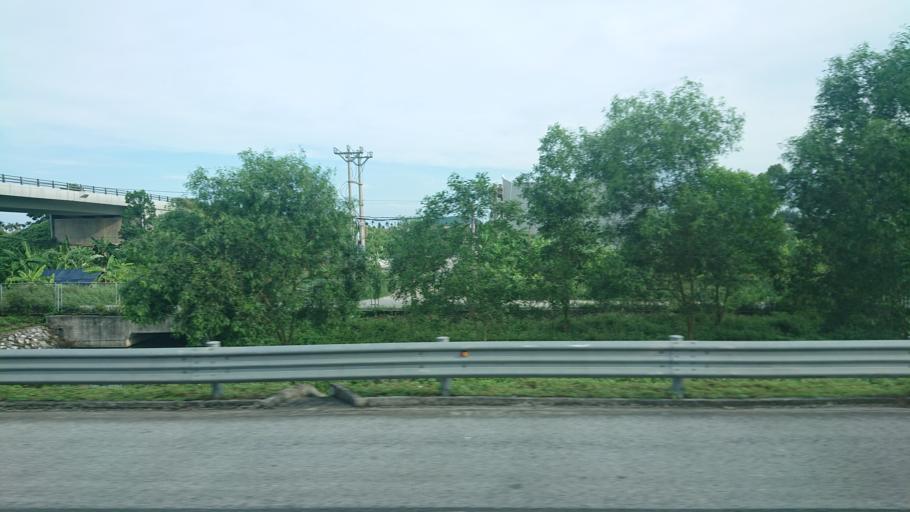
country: VN
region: Hai Phong
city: Nui Doi
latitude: 20.7655
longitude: 106.6601
